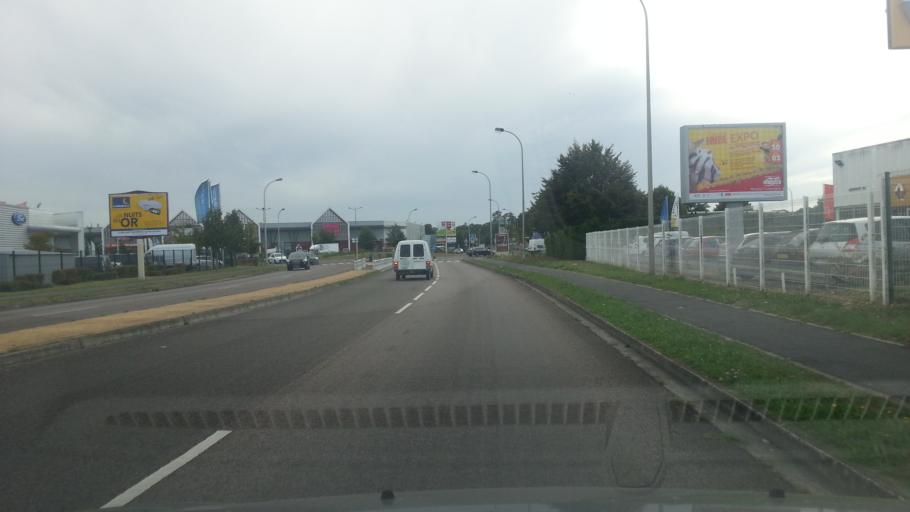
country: FR
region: Picardie
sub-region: Departement de l'Oise
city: Saint-Maximin
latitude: 49.2395
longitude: 2.4647
